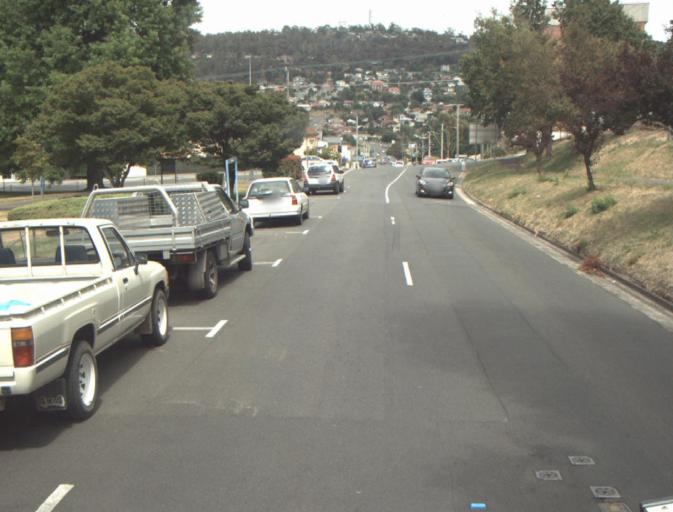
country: AU
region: Tasmania
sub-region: Launceston
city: East Launceston
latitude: -41.4469
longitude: 147.1458
